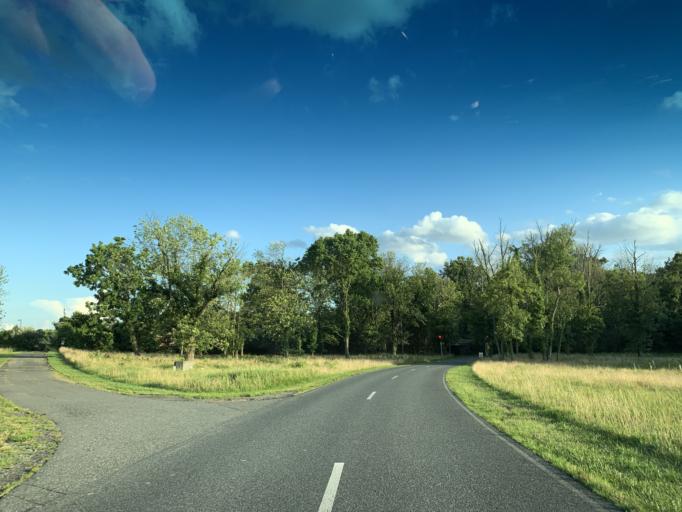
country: US
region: Maryland
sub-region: Harford County
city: Havre de Grace
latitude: 39.5330
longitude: -76.1270
